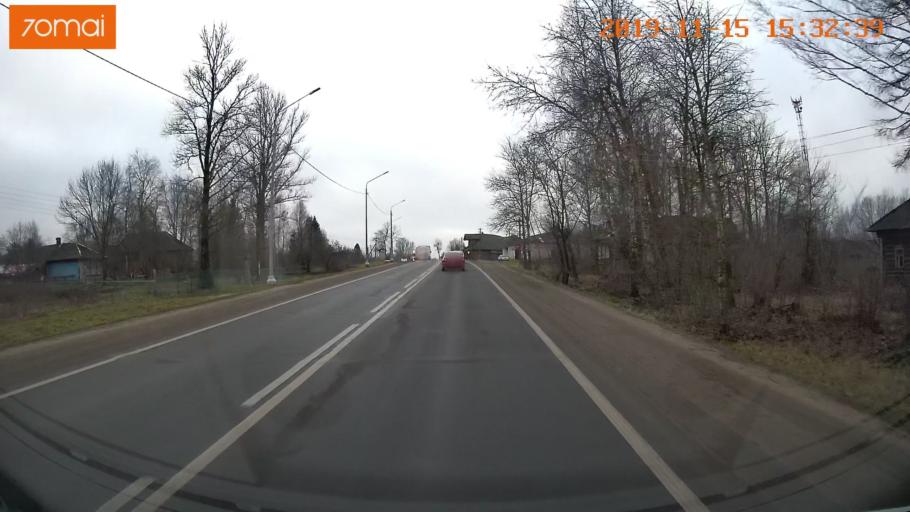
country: RU
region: Jaroslavl
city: Danilov
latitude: 58.0882
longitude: 40.0978
